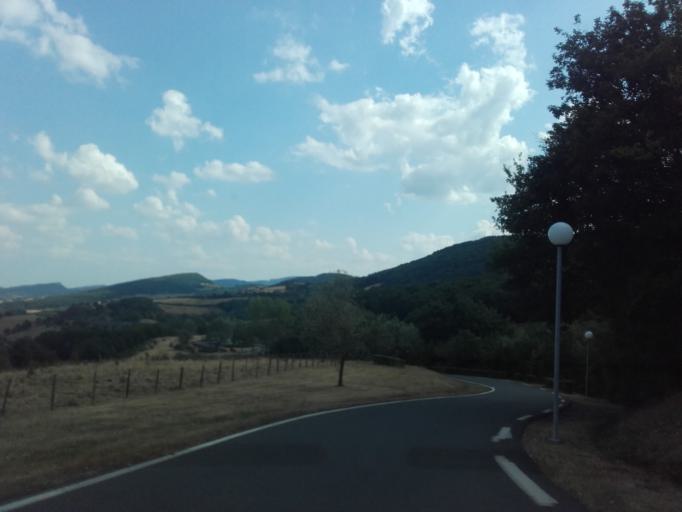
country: FR
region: Bourgogne
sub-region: Departement de Saone-et-Loire
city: Cluny
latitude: 46.3791
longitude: 4.6713
